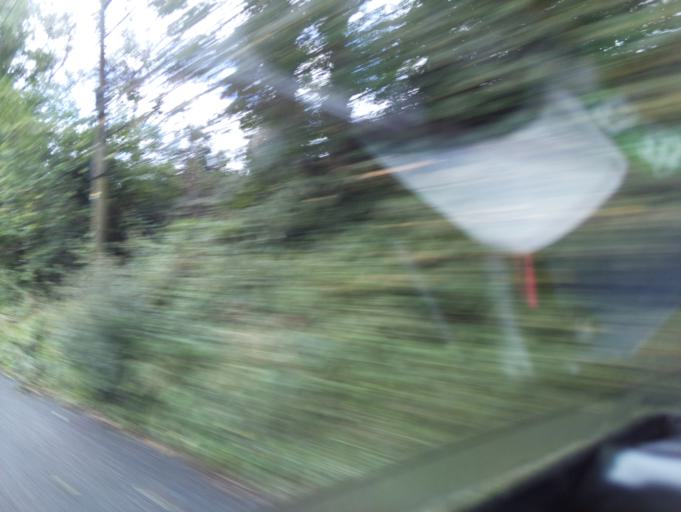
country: GB
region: England
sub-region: Devon
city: Modbury
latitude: 50.3368
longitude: -3.8556
